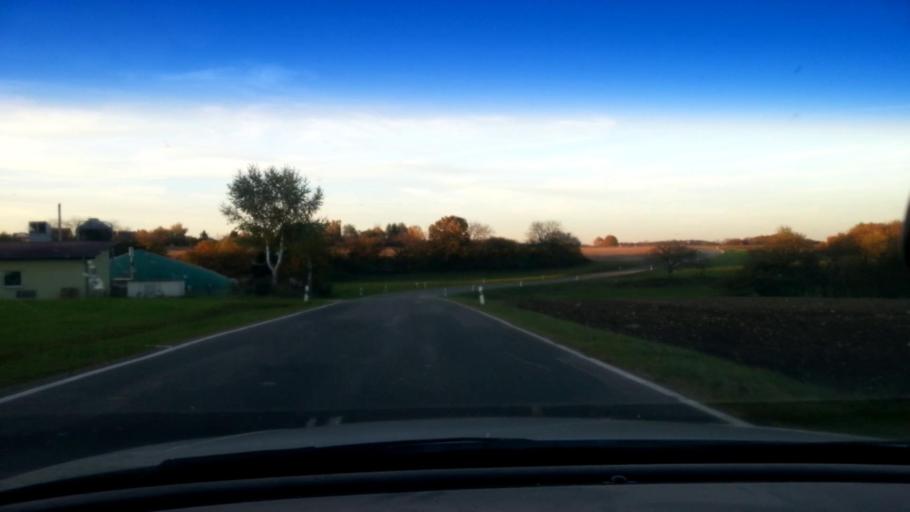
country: DE
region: Bavaria
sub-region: Upper Franconia
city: Heiligenstadt
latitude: 49.8517
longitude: 11.1164
